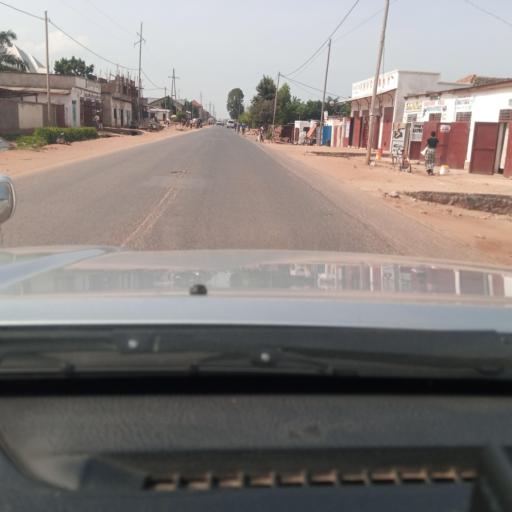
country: BI
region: Bujumbura Mairie
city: Bujumbura
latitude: -3.4600
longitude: 29.3508
